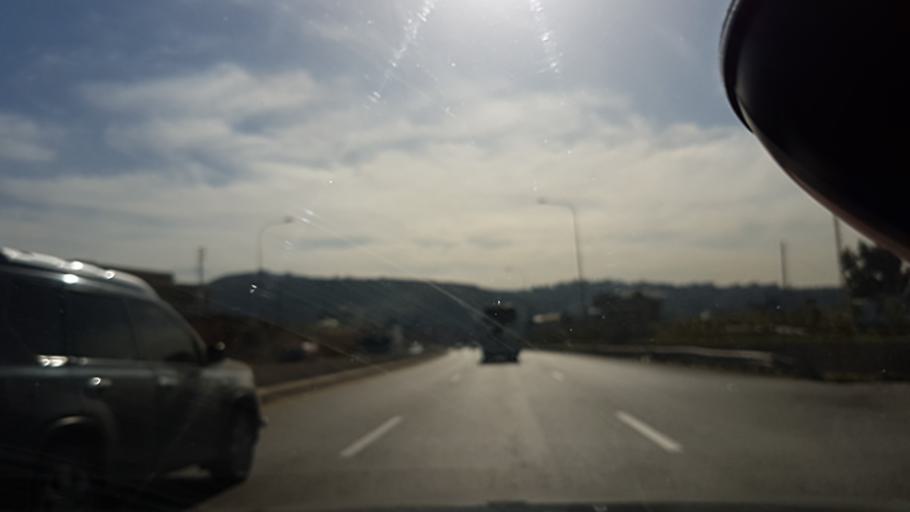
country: LB
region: Liban-Sud
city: Sidon
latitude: 33.6172
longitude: 35.4035
